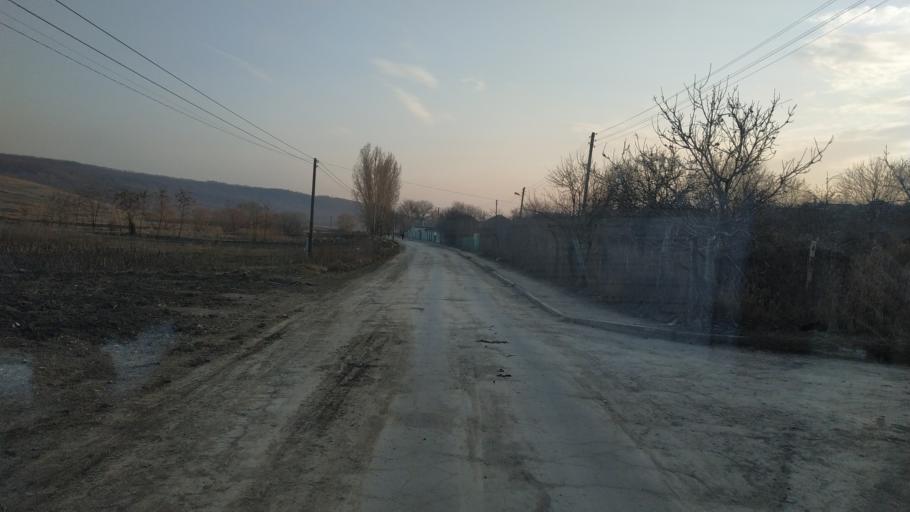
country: MD
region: Hincesti
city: Dancu
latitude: 46.7090
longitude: 28.3452
